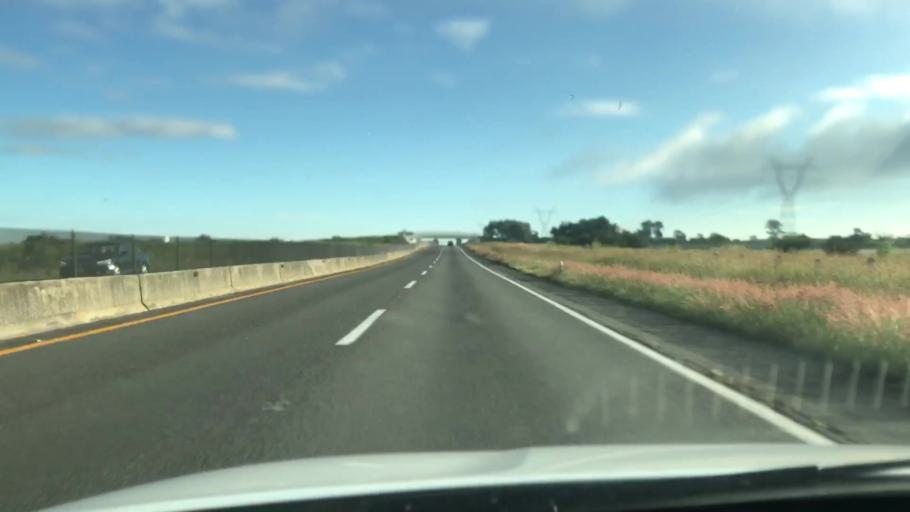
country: MX
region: Jalisco
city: Valle de Guadalupe
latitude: 20.9384
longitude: -102.6559
